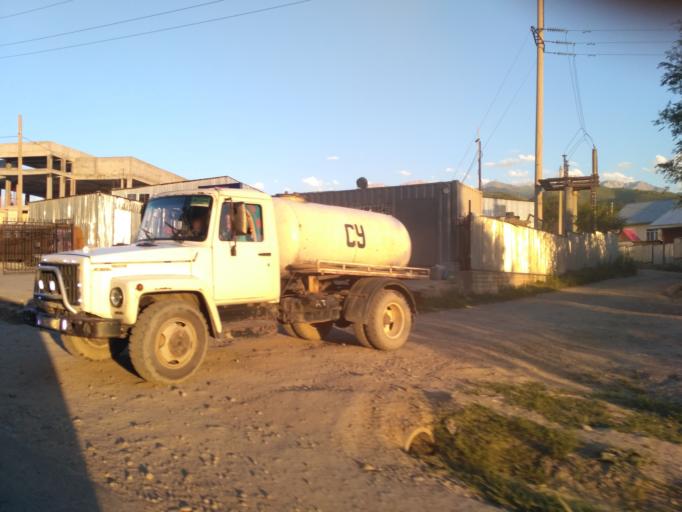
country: KZ
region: Almaty Qalasy
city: Almaty
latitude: 43.1711
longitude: 76.7734
